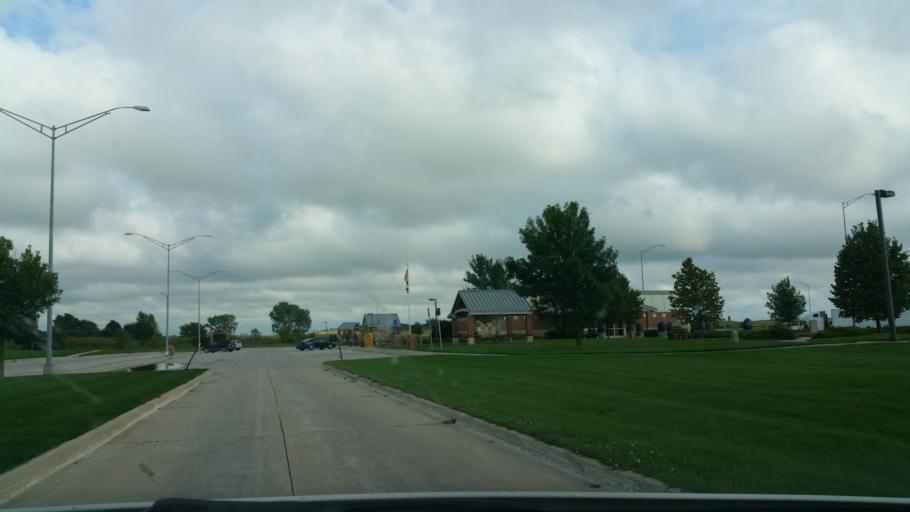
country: US
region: Iowa
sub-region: Franklin County
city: Oakland
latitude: 42.6729
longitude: -93.4612
